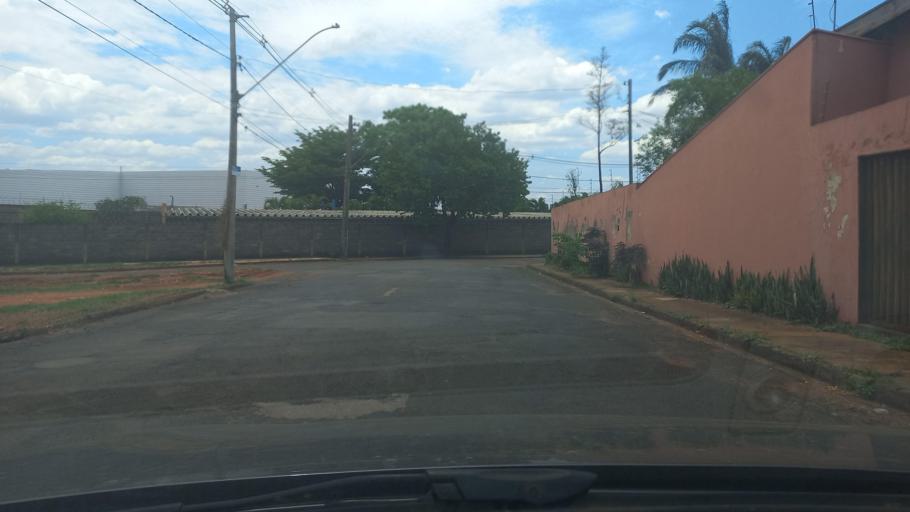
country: BR
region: Minas Gerais
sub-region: Uberaba
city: Uberaba
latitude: -19.7513
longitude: -47.9705
